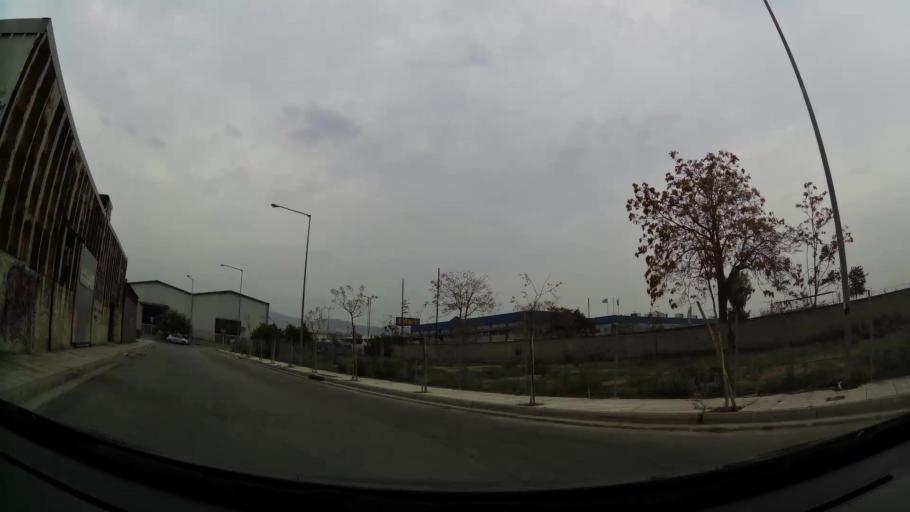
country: GR
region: Attica
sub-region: Nomarchia Athinas
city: Aigaleo
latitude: 37.9728
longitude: 23.6778
